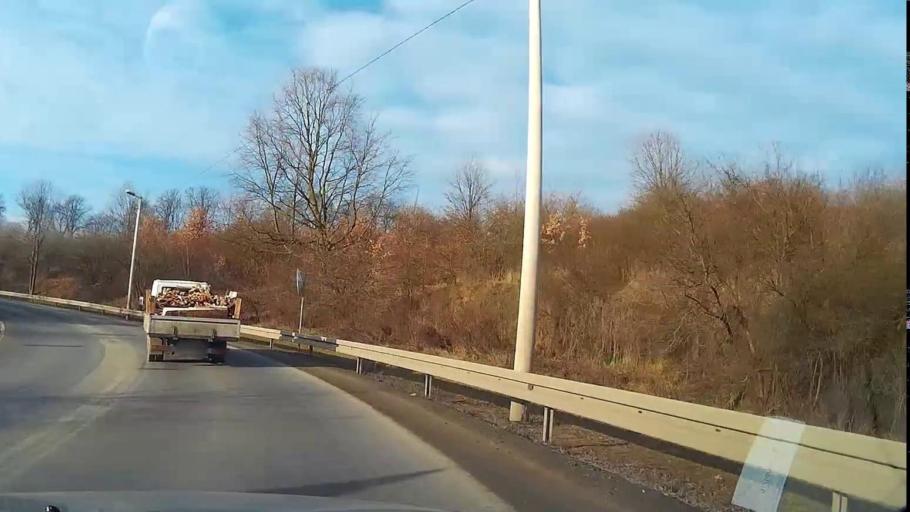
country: PL
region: Lesser Poland Voivodeship
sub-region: Powiat krakowski
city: Kryspinow
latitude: 50.0426
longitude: 19.8360
